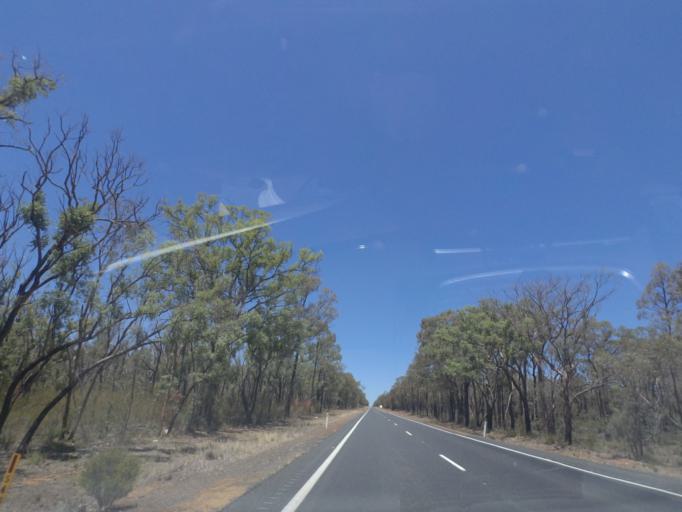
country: AU
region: New South Wales
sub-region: Narrabri
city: Narrabri
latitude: -30.7240
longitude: 149.5240
